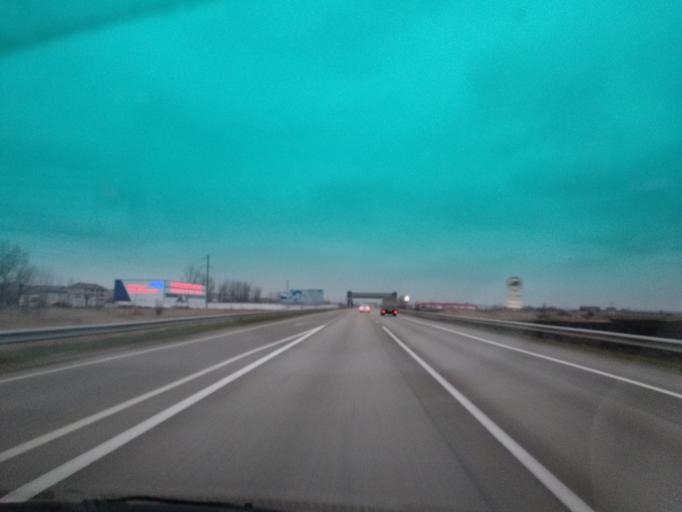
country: RU
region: Adygeya
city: Adygeysk
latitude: 44.8844
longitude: 39.1746
